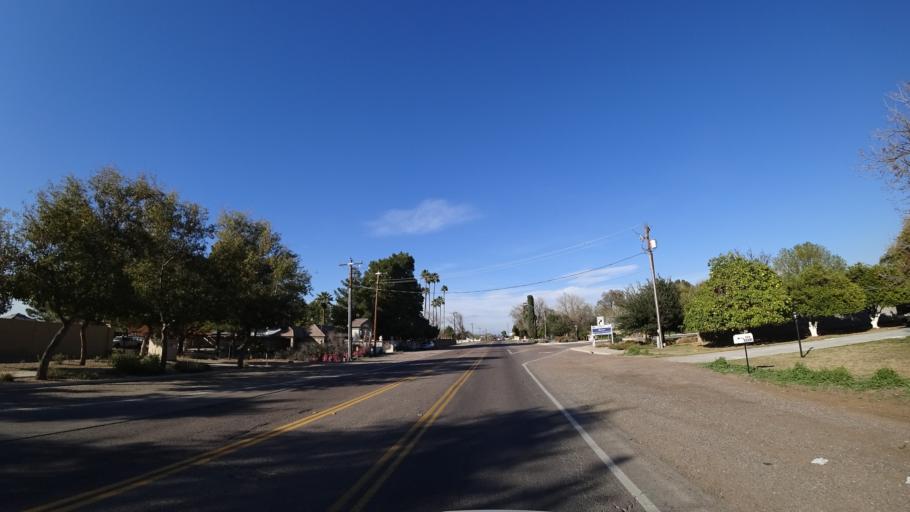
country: US
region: Arizona
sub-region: Maricopa County
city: Peoria
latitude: 33.5482
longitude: -112.2378
